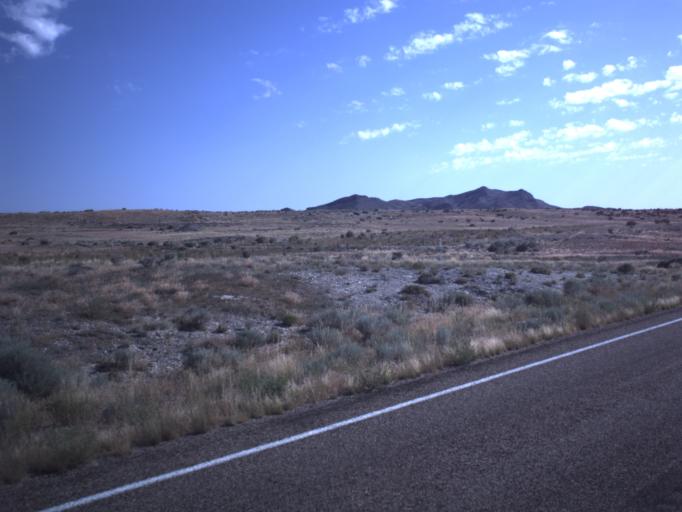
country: US
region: Utah
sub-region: Beaver County
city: Milford
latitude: 38.7891
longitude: -112.9132
